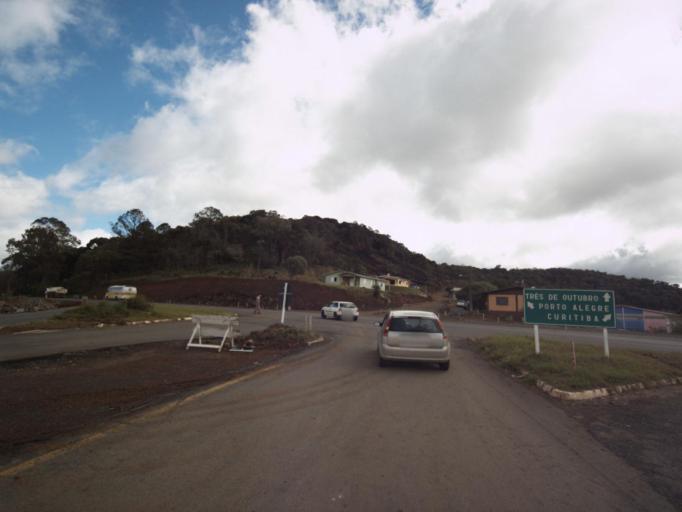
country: BR
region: Santa Catarina
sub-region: Concordia
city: Concordia
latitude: -27.1811
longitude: -51.9178
